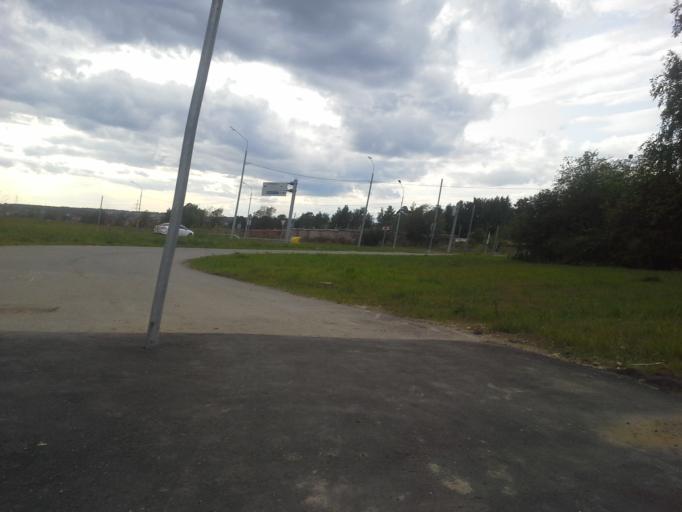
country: RU
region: Moskovskaya
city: Kokoshkino
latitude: 55.5962
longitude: 37.1596
